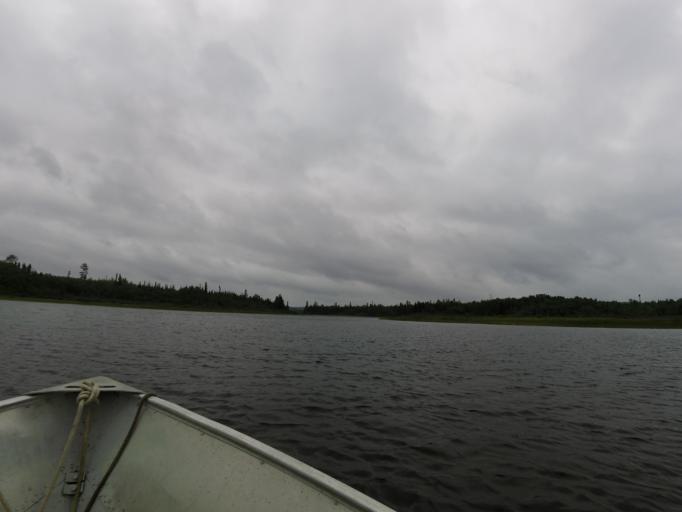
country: CA
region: Ontario
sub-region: Rainy River District
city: Atikokan
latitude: 49.5981
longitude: -91.3421
